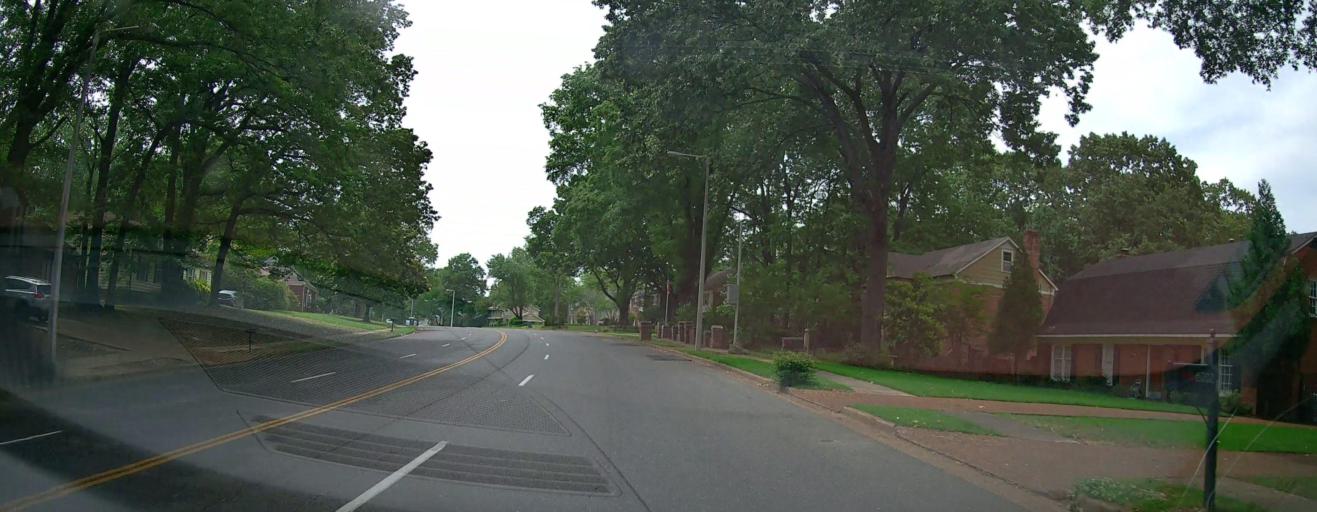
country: US
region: Tennessee
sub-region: Shelby County
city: Germantown
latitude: 35.0855
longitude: -89.8540
